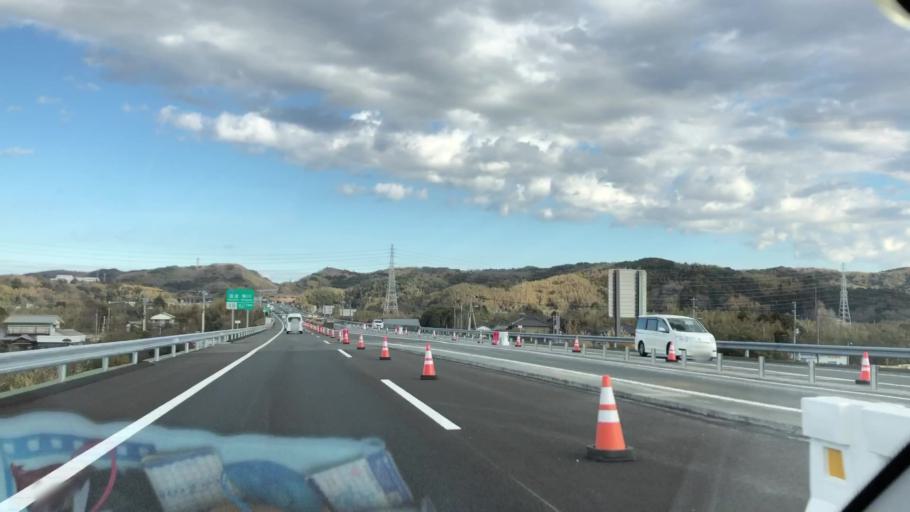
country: JP
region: Chiba
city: Kimitsu
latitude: 35.3069
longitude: 139.9418
